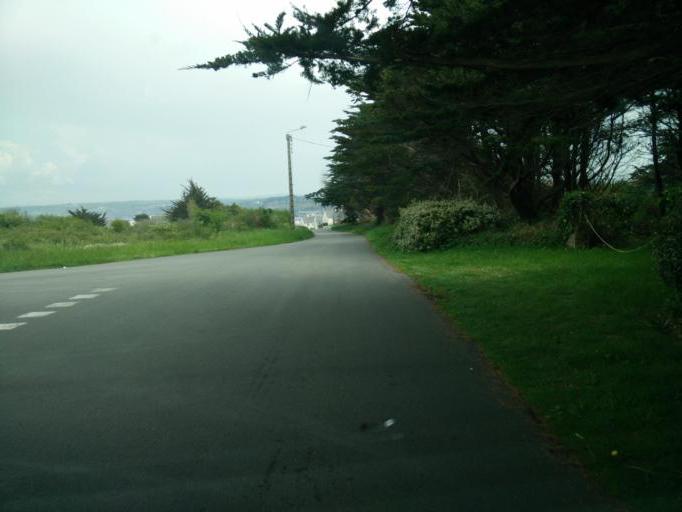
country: FR
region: Brittany
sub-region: Departement du Finistere
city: Camaret-sur-Mer
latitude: 48.2805
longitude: -4.6092
